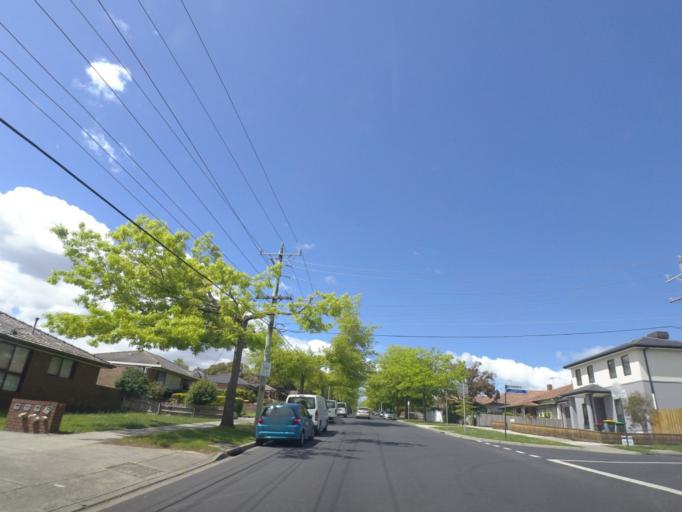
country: AU
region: Victoria
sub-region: Whitehorse
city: Box Hill
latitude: -37.8140
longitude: 145.1272
